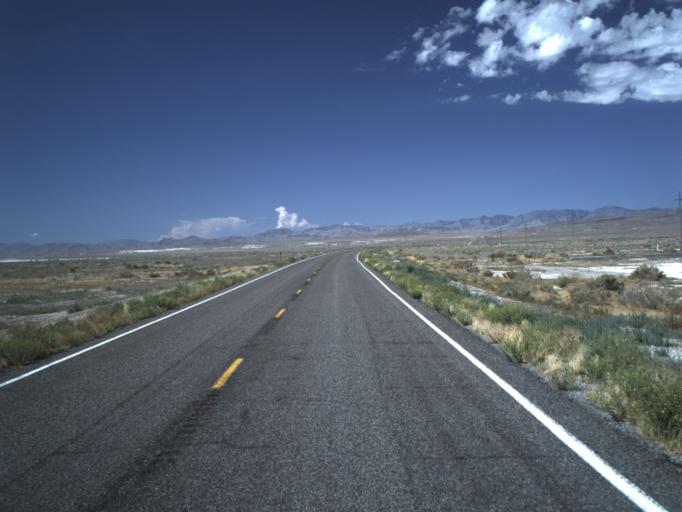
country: US
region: Utah
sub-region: Millard County
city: Delta
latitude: 39.0944
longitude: -113.1647
